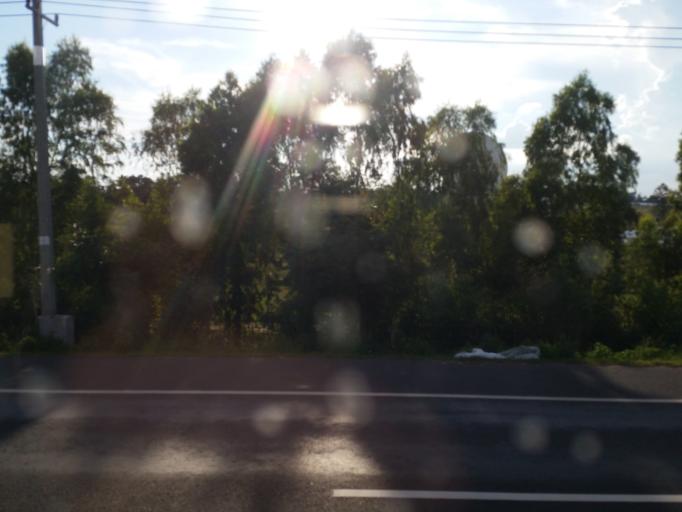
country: TH
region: Changwat Ubon Ratchathani
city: Sirindhorn
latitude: 15.1935
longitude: 105.3684
